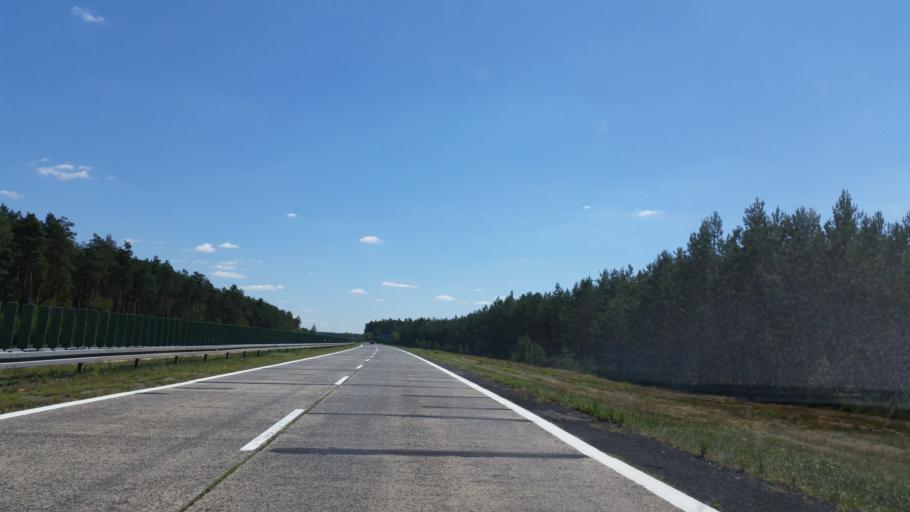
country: PL
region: Lower Silesian Voivodeship
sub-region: Powiat boleslawiecki
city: Boleslawiec
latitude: 51.3696
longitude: 15.5669
